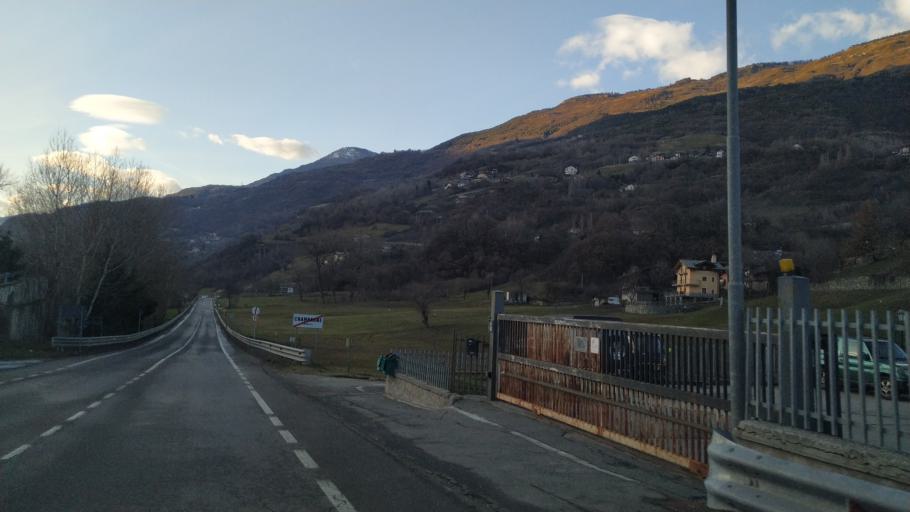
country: IT
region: Aosta Valley
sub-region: Valle d'Aosta
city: Chez Croiset
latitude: 45.7439
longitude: 7.5146
